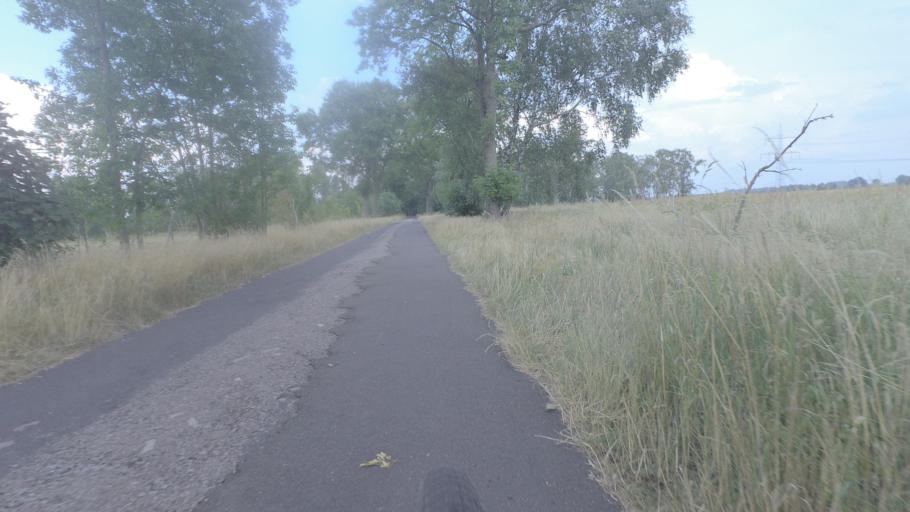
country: DE
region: Brandenburg
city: Trebbin
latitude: 52.2695
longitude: 13.1367
